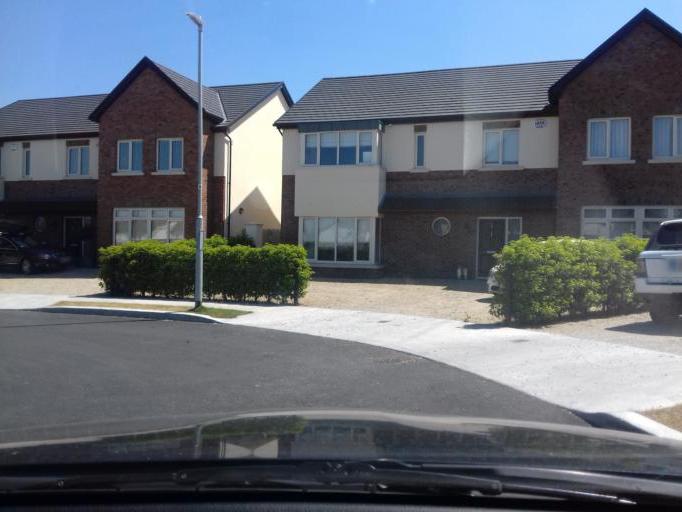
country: IE
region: Leinster
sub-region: Fingal County
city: Swords
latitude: 53.5161
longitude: -6.2640
